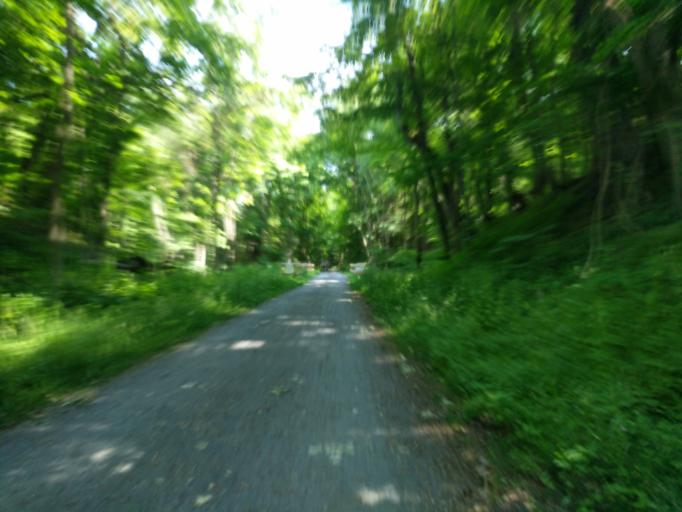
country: US
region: New York
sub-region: Tompkins County
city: Northwest Ithaca
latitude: 42.4859
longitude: -76.5384
